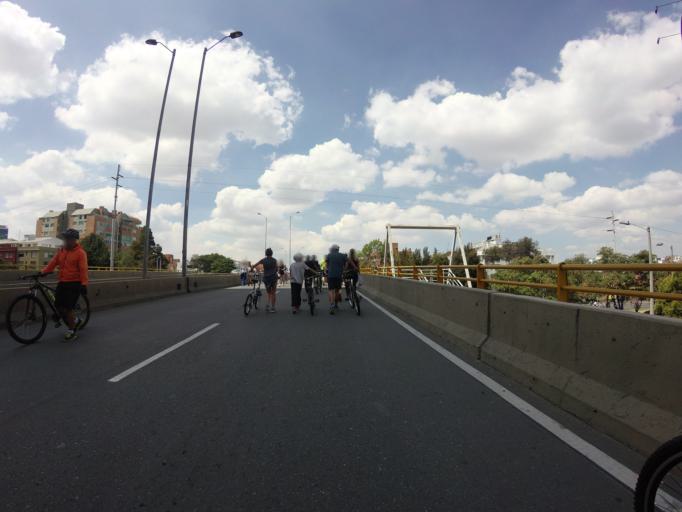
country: CO
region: Bogota D.C.
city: Barrio San Luis
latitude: 4.6941
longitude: -74.0341
